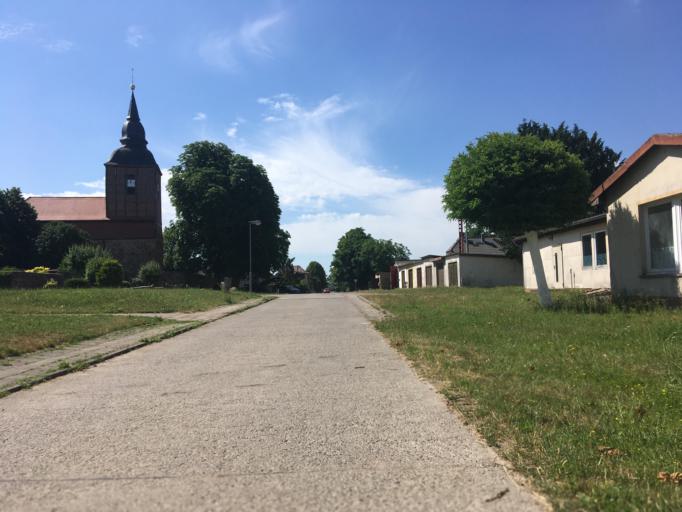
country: DE
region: Brandenburg
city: Goritz
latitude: 53.4413
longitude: 13.9213
